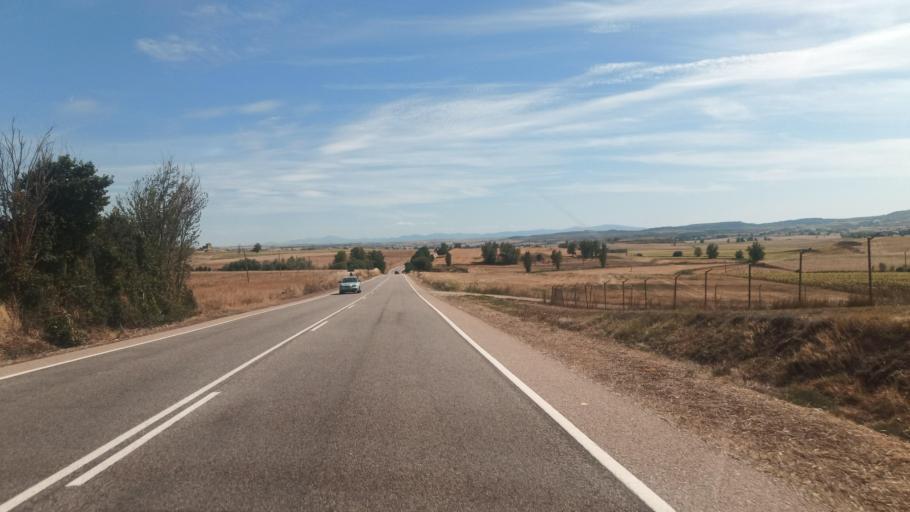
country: ES
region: Castille and Leon
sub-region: Provincia de Burgos
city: Quintanabureba
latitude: 42.6296
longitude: -3.3758
